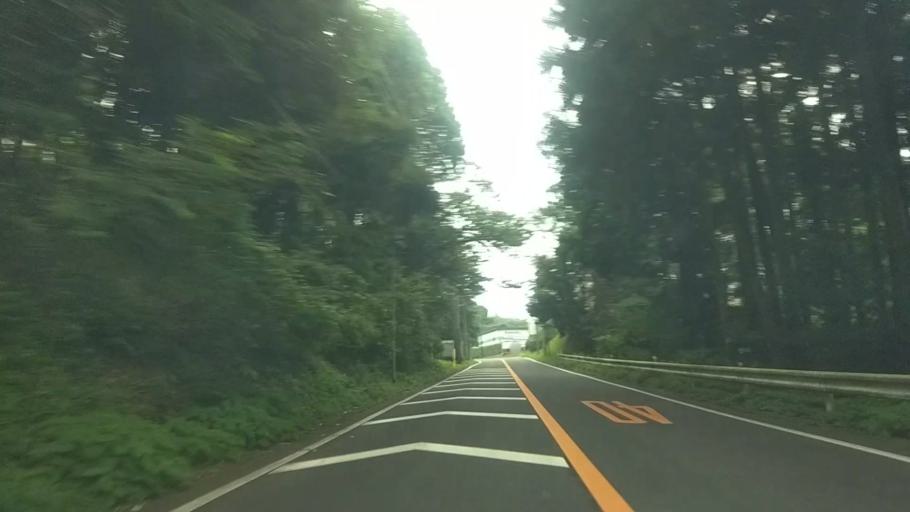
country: JP
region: Chiba
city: Kawaguchi
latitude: 35.2190
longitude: 140.0744
